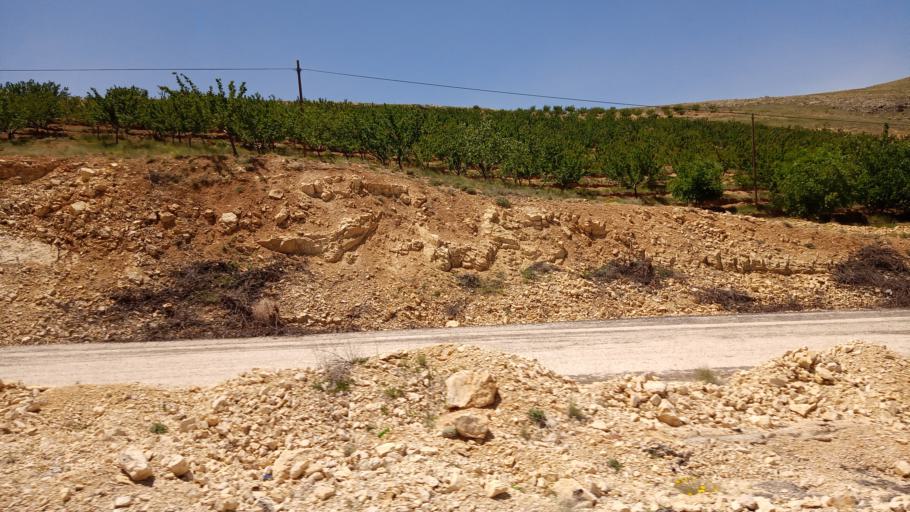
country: TR
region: Malatya
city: Darende
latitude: 38.6343
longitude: 37.4514
